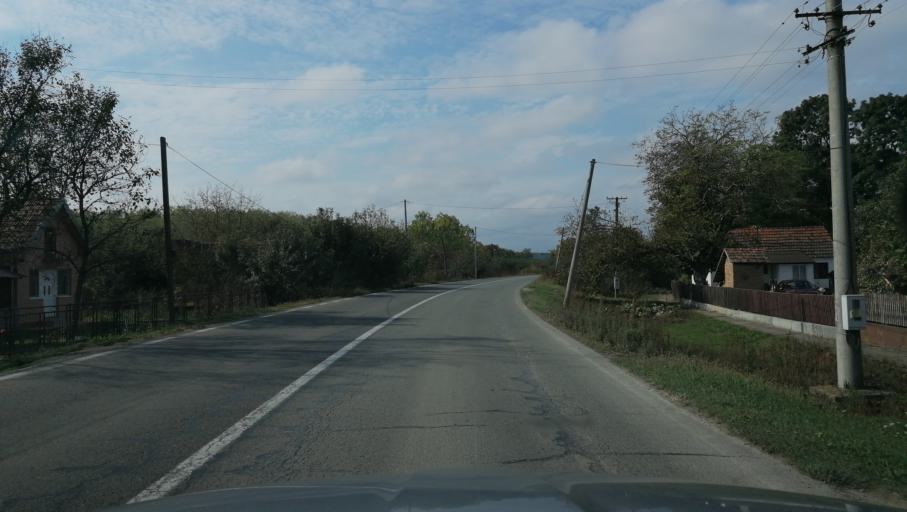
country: RS
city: Bosut
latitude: 44.9236
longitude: 19.3486
